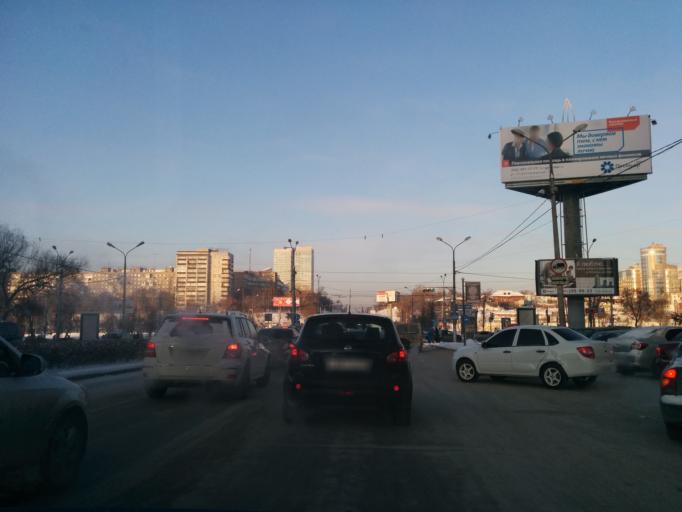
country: RU
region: Perm
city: Perm
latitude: 58.0084
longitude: 56.2276
